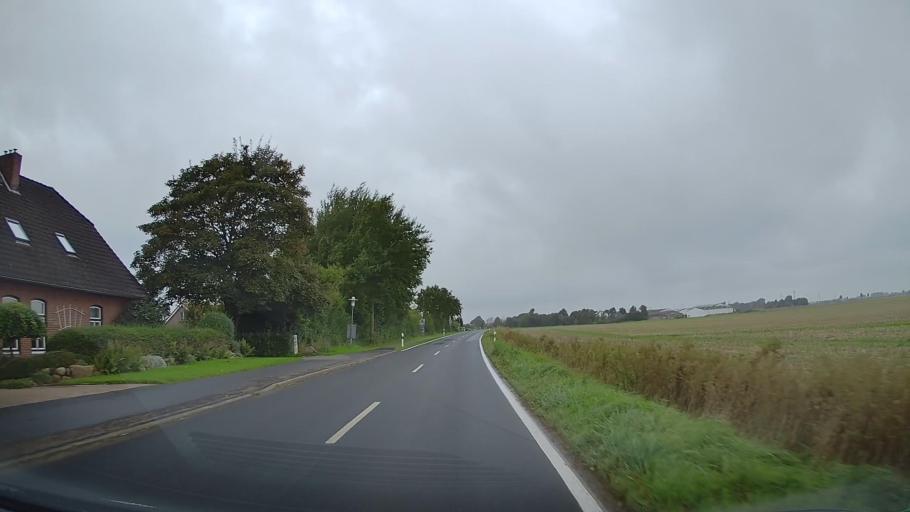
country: DE
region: Schleswig-Holstein
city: Friedrichsgabekoog
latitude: 54.1421
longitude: 8.9256
